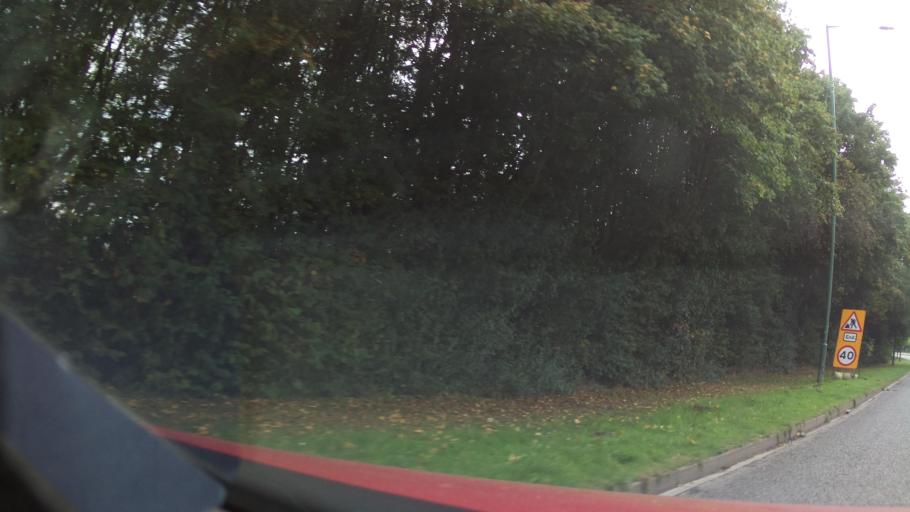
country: GB
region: England
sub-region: Solihull
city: Bickenhill
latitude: 52.4629
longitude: -1.7159
